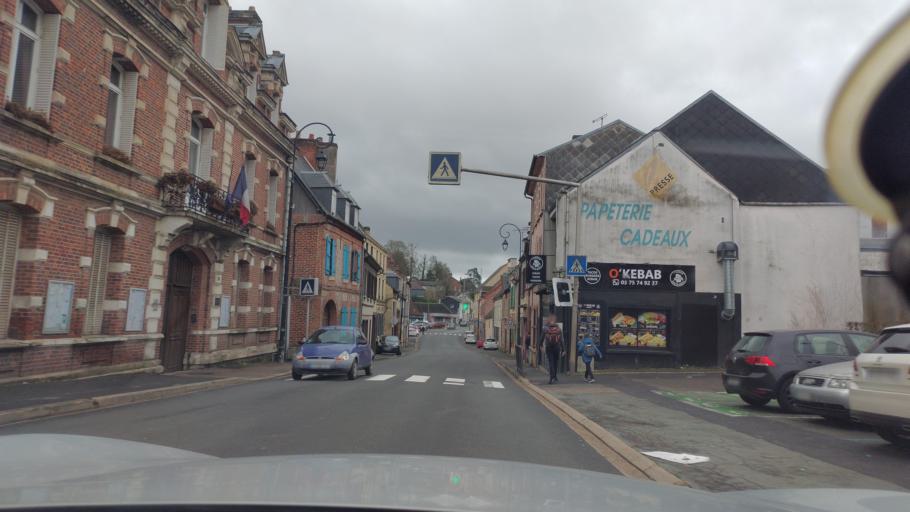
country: FR
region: Picardie
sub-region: Departement de l'Oise
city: Saint-Omer-en-Chaussee
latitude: 49.5756
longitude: 1.9551
